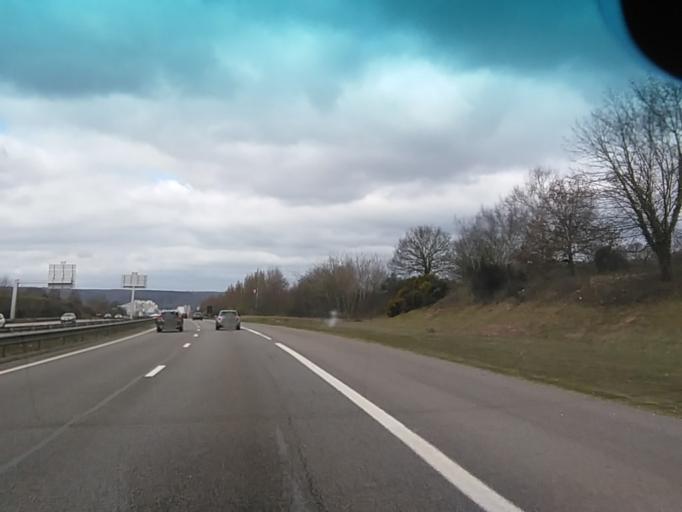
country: FR
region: Haute-Normandie
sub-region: Departement de la Seine-Maritime
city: Le Grand-Quevilly
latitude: 49.3892
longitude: 1.0449
